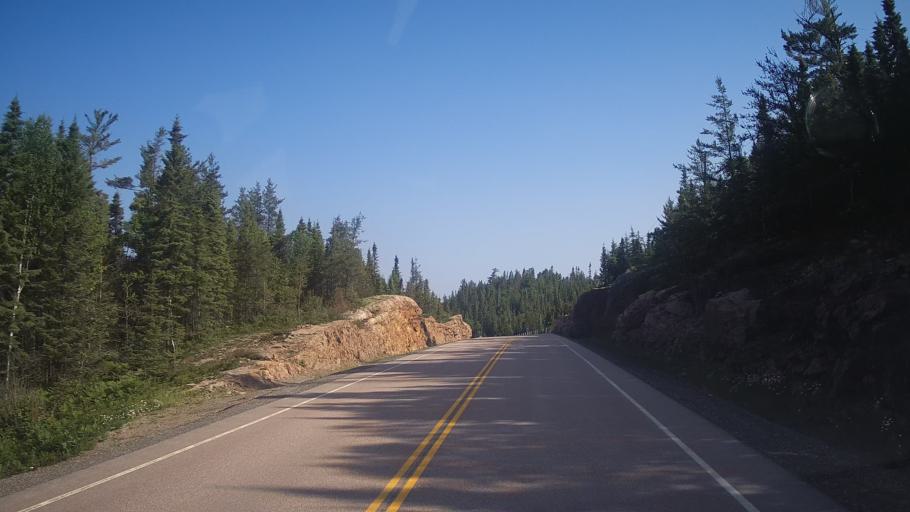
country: CA
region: Ontario
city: Rayside-Balfour
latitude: 47.0109
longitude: -81.6337
